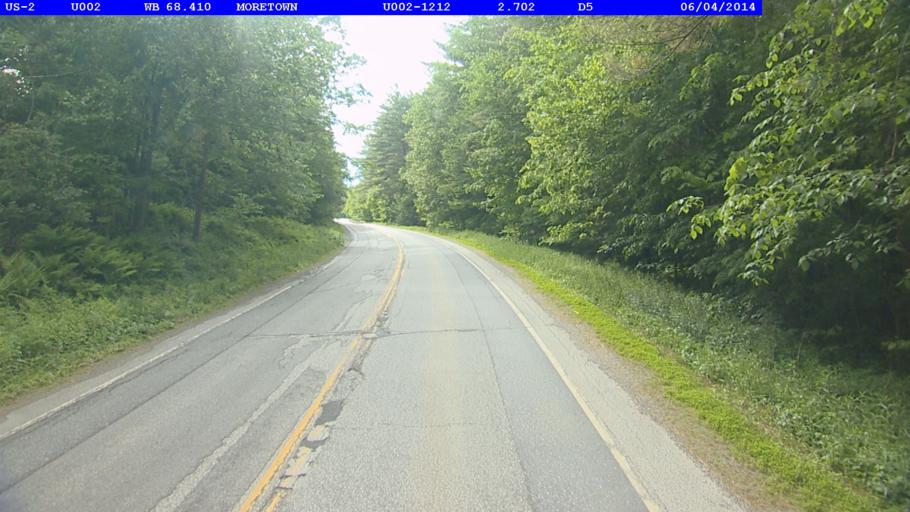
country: US
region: Vermont
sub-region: Washington County
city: Waterbury
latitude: 44.3126
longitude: -72.7013
